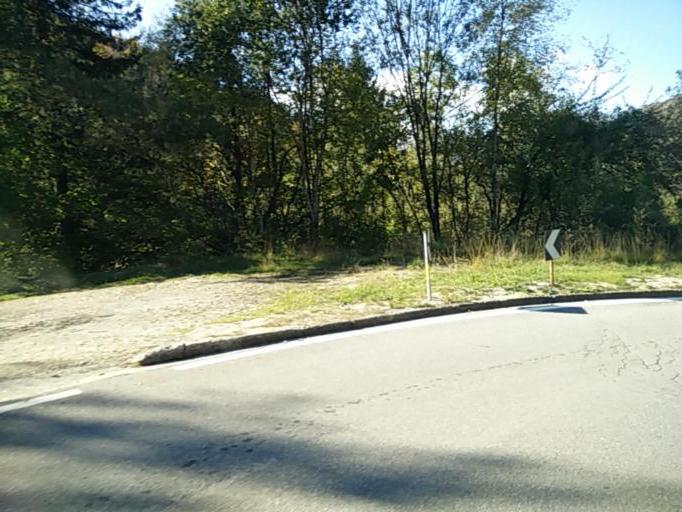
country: IT
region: Lombardy
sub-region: Provincia di Brescia
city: Capovalle
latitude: 45.7466
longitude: 10.5235
